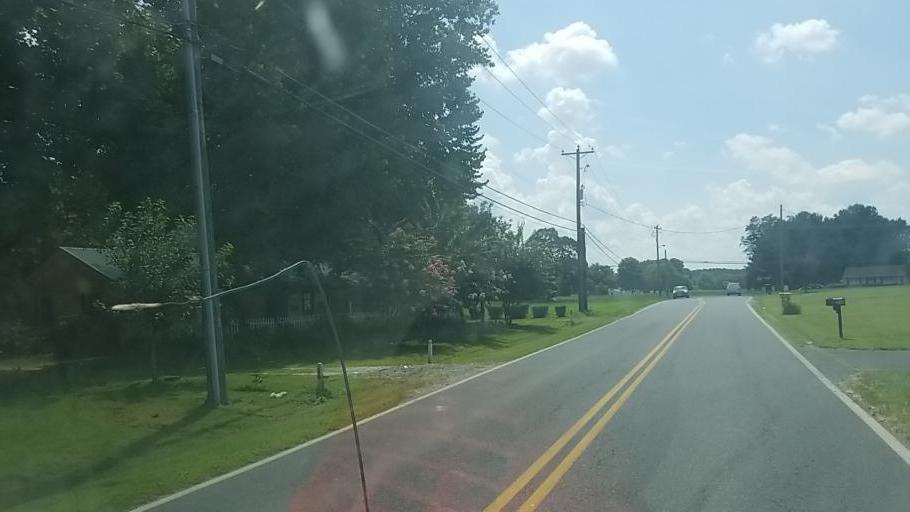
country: US
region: Maryland
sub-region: Wicomico County
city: Salisbury
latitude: 38.3610
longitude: -75.5482
